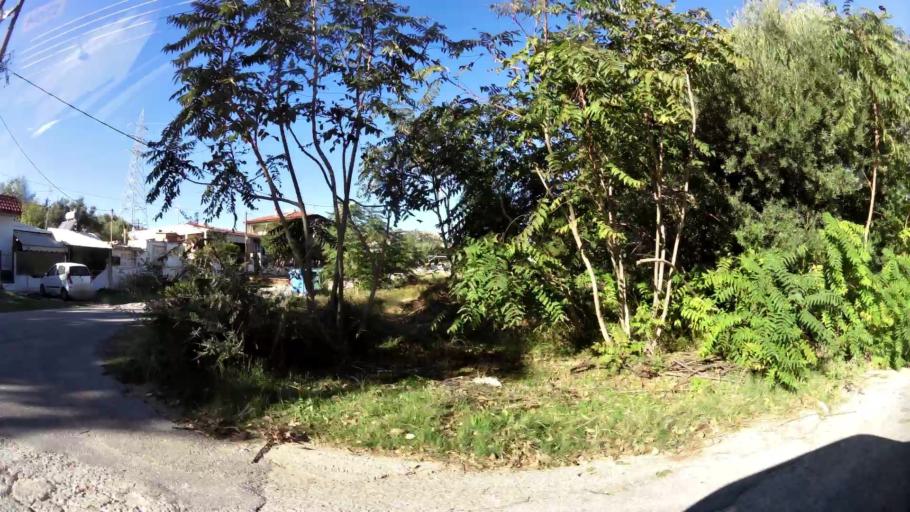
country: GR
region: Attica
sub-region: Nomarchia Anatolikis Attikis
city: Leondarion
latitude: 37.9927
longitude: 23.8446
